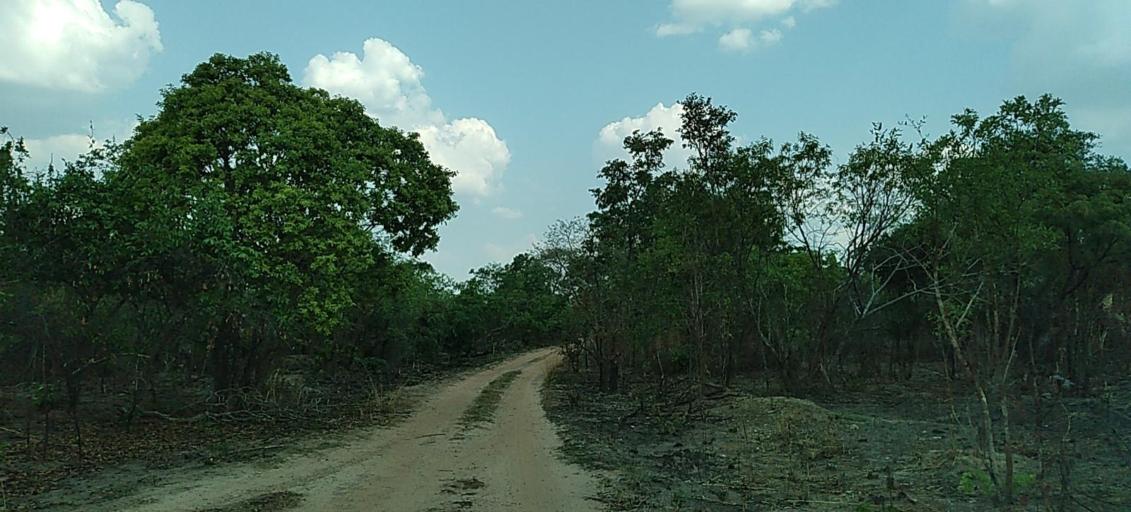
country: ZM
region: Copperbelt
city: Luanshya
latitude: -13.1580
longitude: 28.3328
